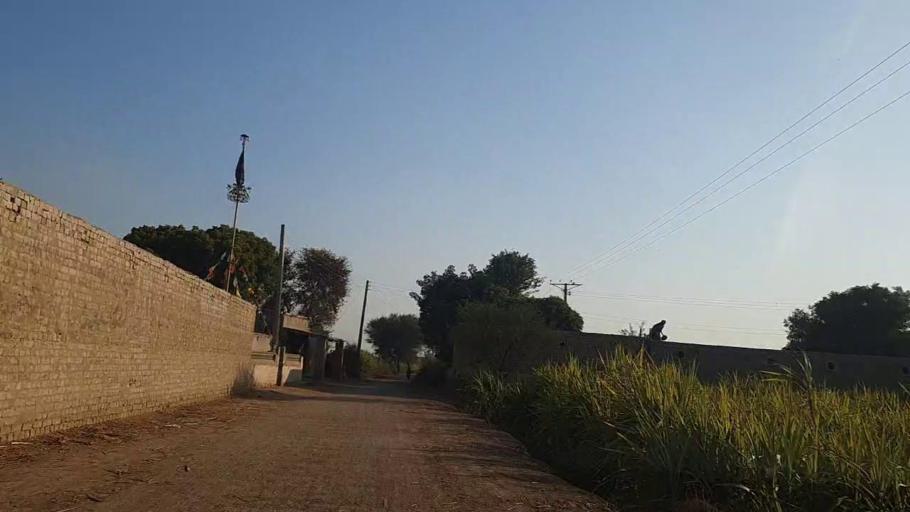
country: PK
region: Sindh
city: Sakrand
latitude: 26.3072
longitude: 68.1430
